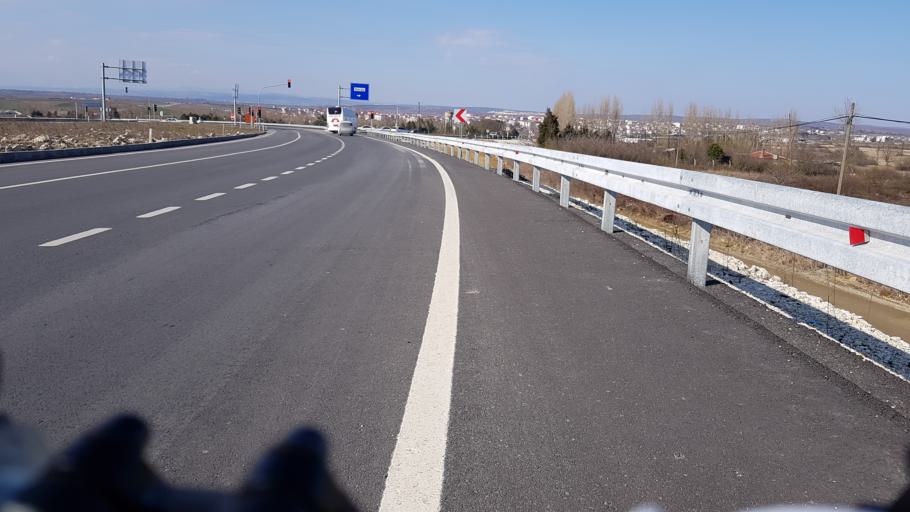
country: TR
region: Tekirdag
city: Saray
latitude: 41.4170
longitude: 27.9222
